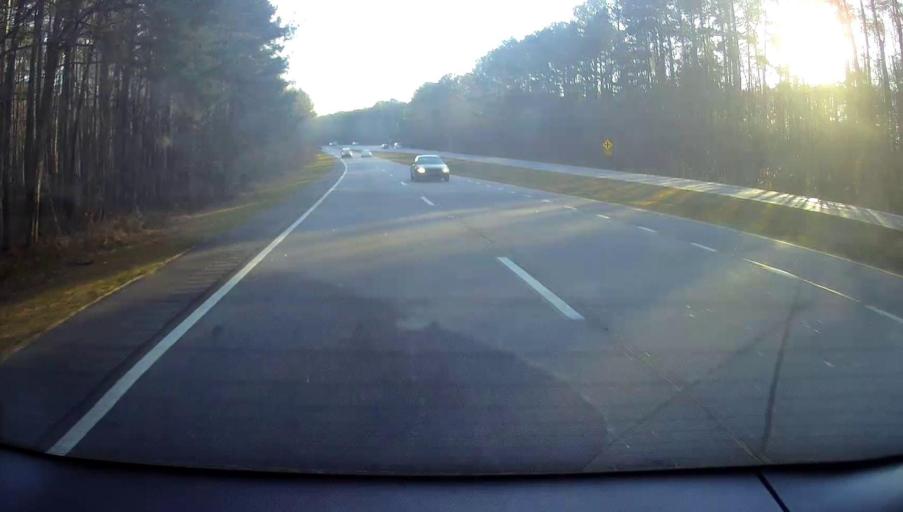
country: US
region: Georgia
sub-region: Fayette County
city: Peachtree City
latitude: 33.4269
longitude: -84.6028
